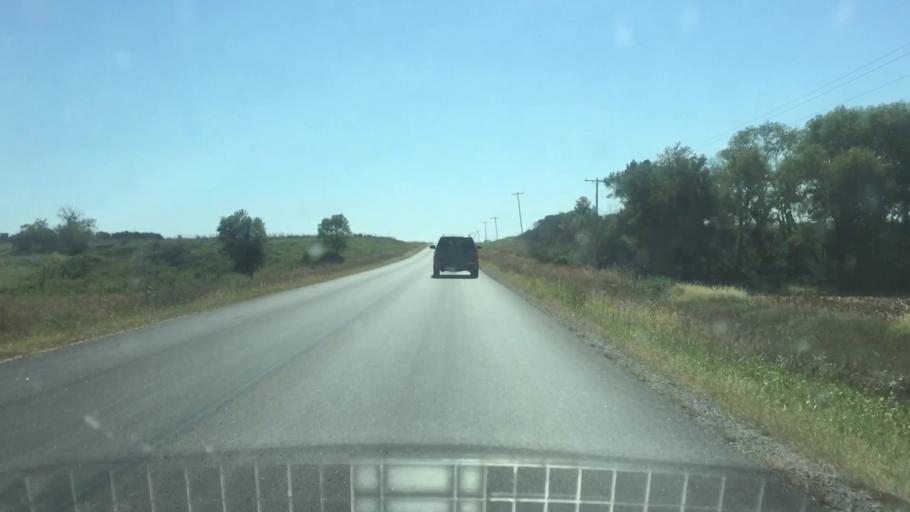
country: US
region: Kansas
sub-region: Marshall County
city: Marysville
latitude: 39.8768
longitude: -96.6009
